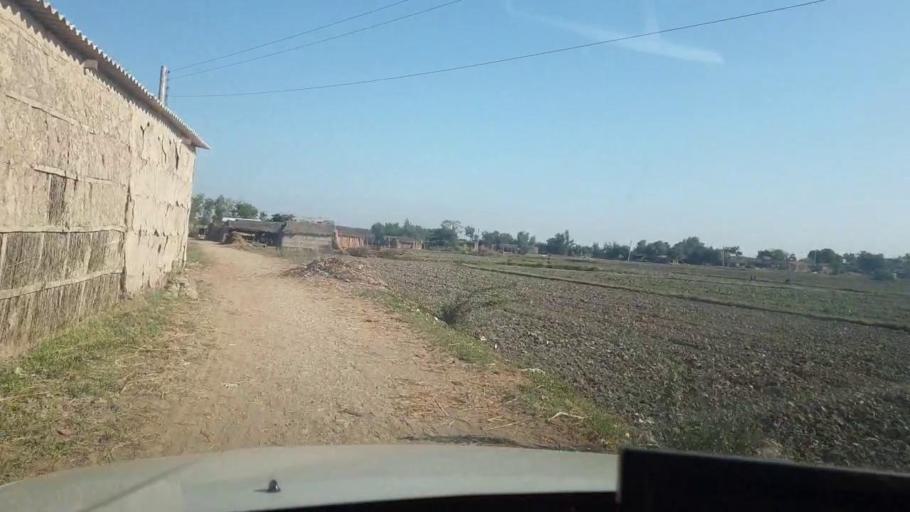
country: PK
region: Sindh
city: Mirpur Sakro
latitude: 24.4948
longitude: 67.6323
